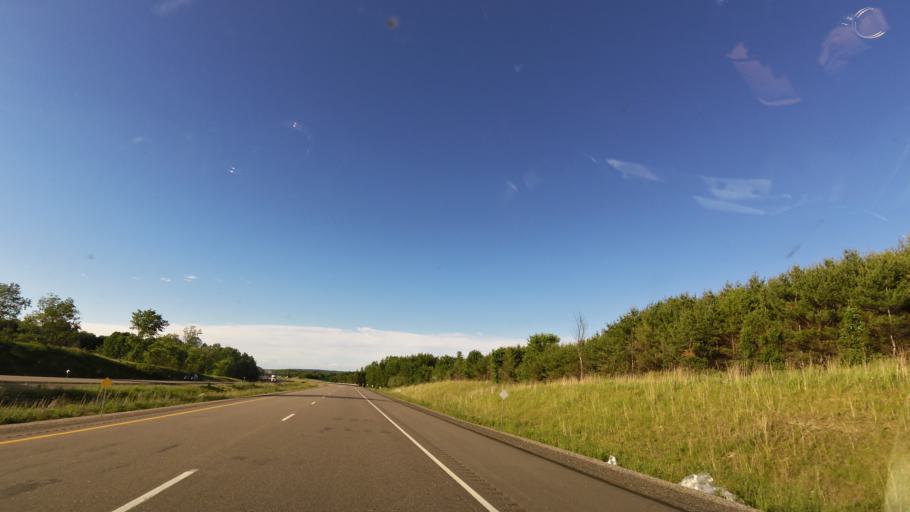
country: CA
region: Ontario
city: Barrie
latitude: 44.6137
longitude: -79.6652
